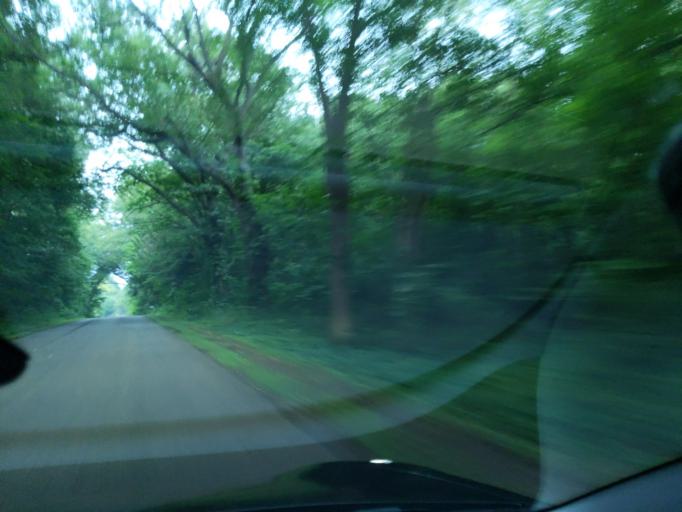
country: US
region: Michigan
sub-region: Ingham County
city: Leslie
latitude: 42.3495
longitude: -84.5050
